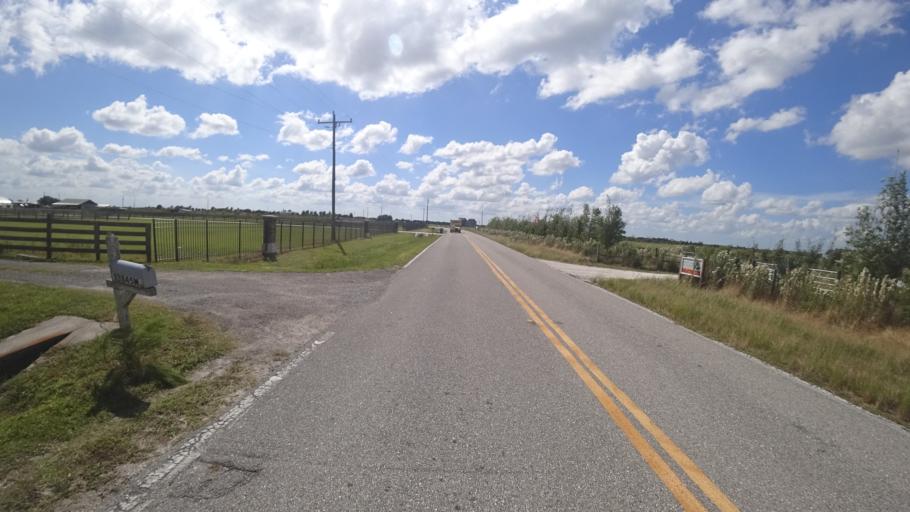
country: US
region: Florida
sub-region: Sarasota County
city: Lake Sarasota
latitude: 27.3029
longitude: -82.1870
